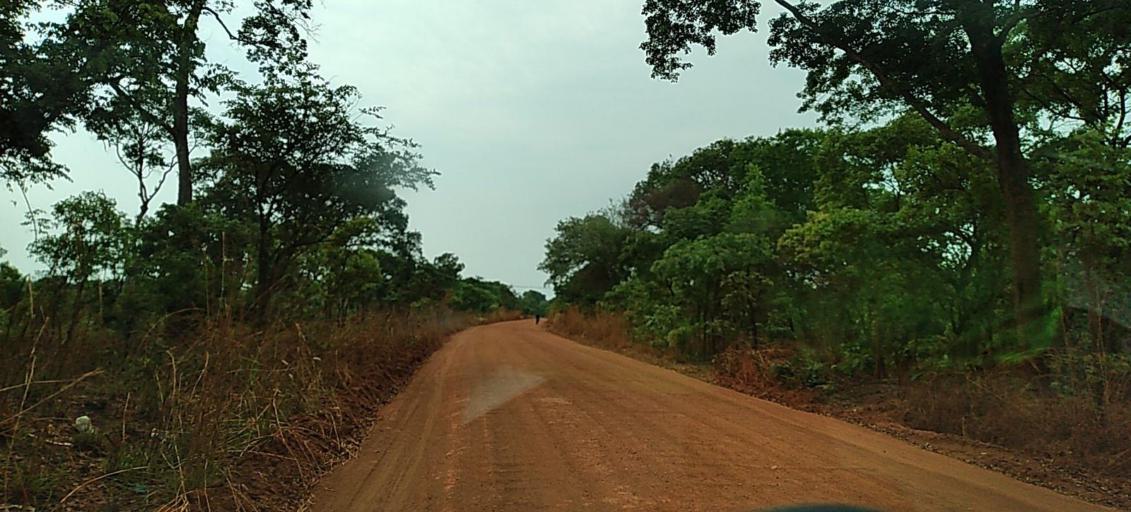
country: ZM
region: North-Western
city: Solwezi
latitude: -12.2130
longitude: 26.5042
